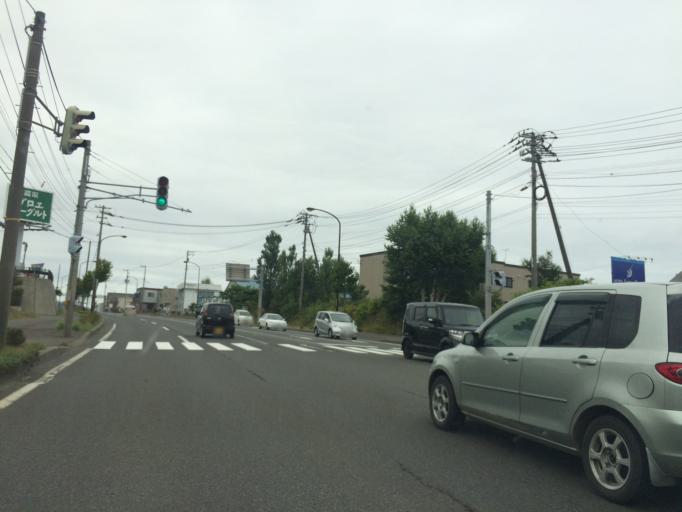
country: JP
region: Hokkaido
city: Otaru
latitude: 43.1418
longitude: 141.1503
